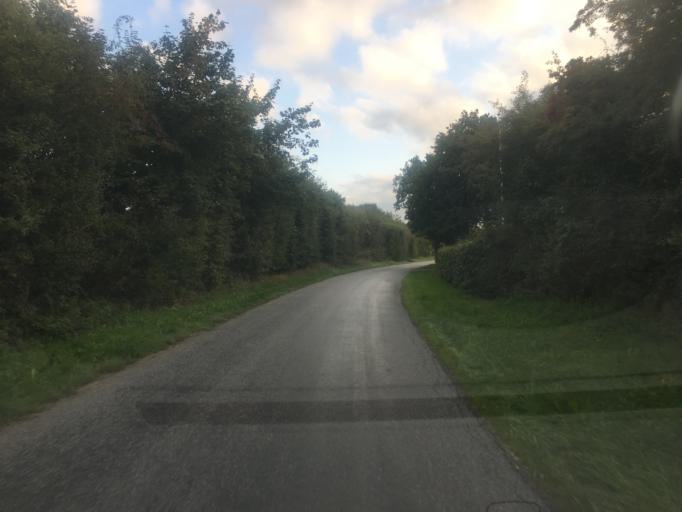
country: DK
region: South Denmark
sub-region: Tonder Kommune
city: Logumkloster
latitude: 55.0474
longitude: 8.9409
